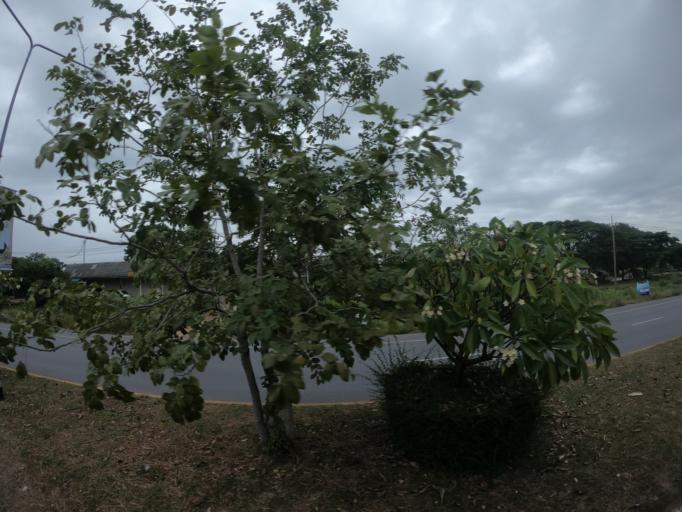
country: TH
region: Maha Sarakham
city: Maha Sarakham
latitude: 16.1664
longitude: 103.2870
